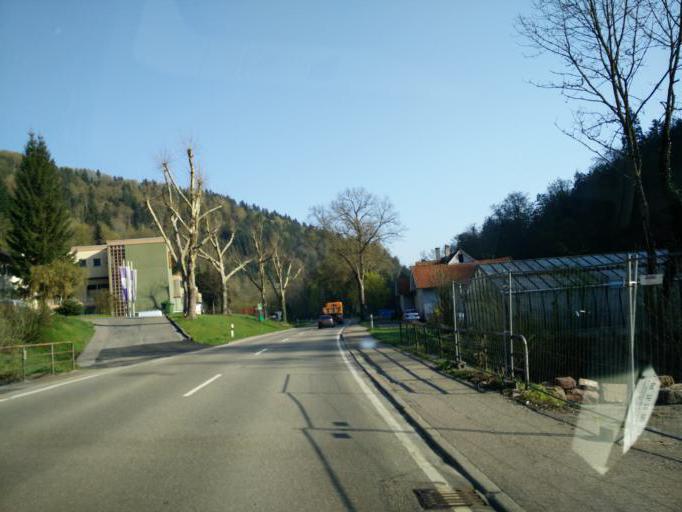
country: DE
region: Baden-Wuerttemberg
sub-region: Karlsruhe Region
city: Bad Liebenzell
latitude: 48.7611
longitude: 8.7296
